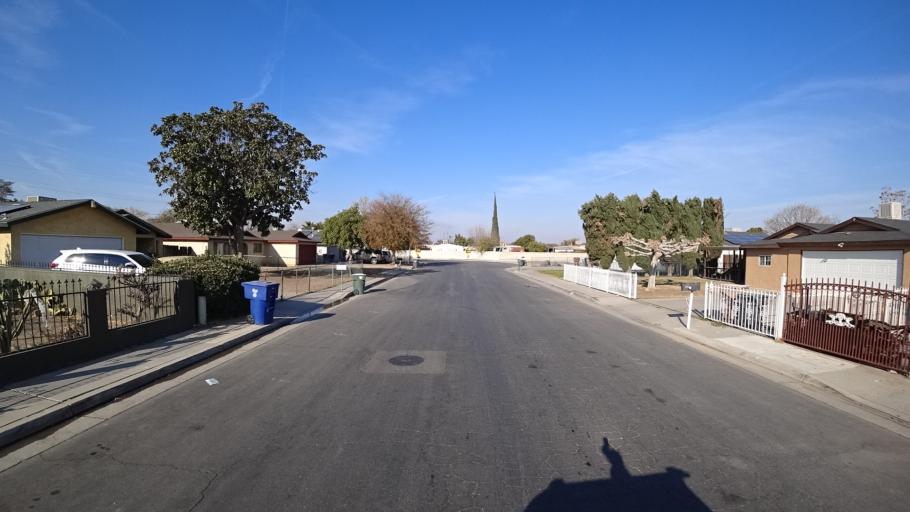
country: US
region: California
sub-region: Kern County
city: Greenfield
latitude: 35.3207
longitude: -119.0090
